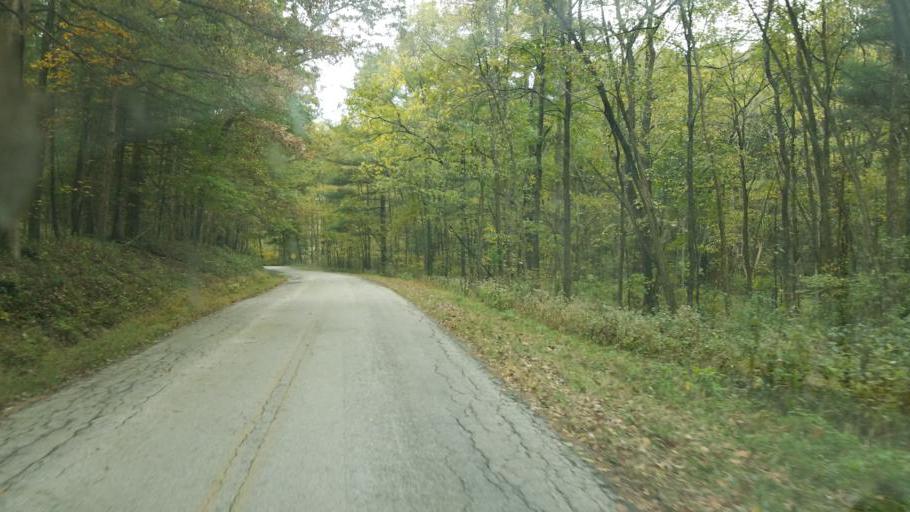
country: US
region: Ohio
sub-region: Ashland County
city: Loudonville
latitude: 40.5598
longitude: -82.1521
